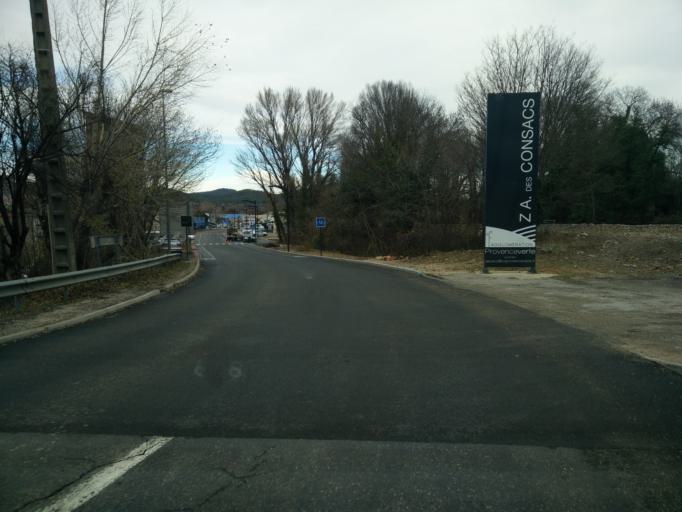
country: FR
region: Provence-Alpes-Cote d'Azur
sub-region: Departement du Var
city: La Celle
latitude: 43.3964
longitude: 6.0464
